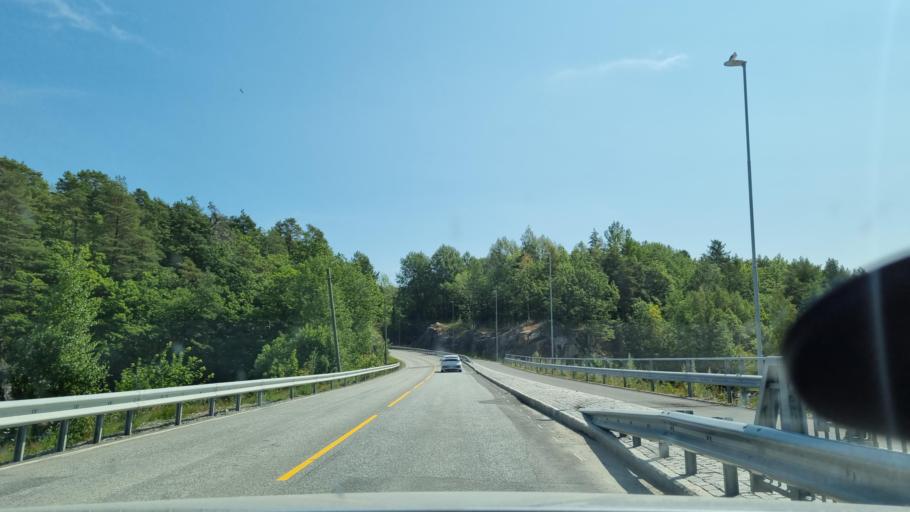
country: NO
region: Aust-Agder
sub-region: Arendal
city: Arendal
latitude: 58.4664
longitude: 8.8295
